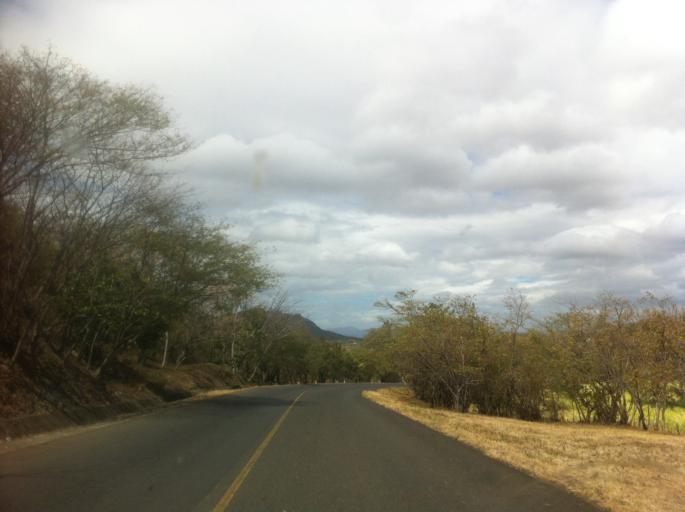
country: NI
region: Chontales
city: Juigalpa
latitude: 12.0430
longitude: -85.2790
